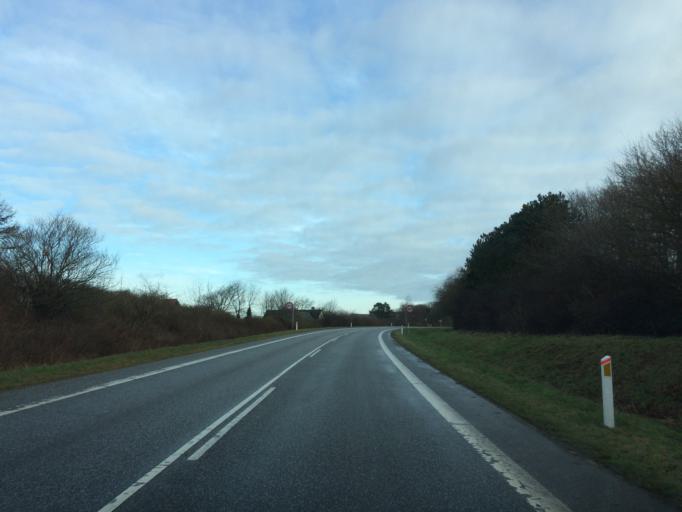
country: DK
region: Central Jutland
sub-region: Struer Kommune
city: Struer
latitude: 56.4896
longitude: 8.5654
